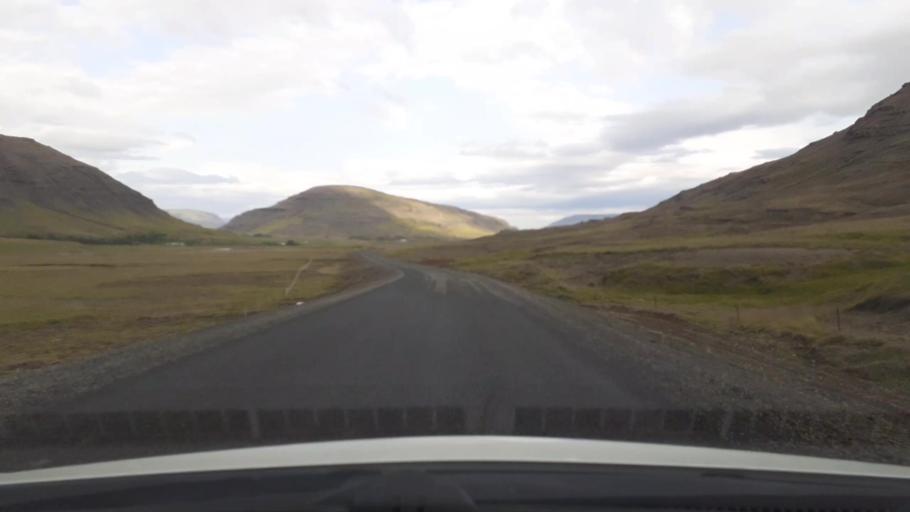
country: IS
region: Capital Region
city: Mosfellsbaer
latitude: 64.2976
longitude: -21.4689
